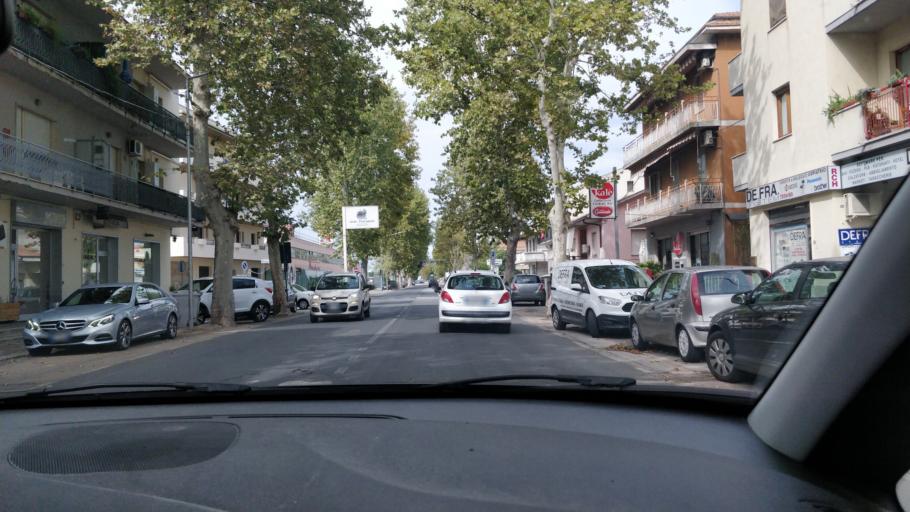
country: IT
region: Abruzzo
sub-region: Provincia di Chieti
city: Sambuceto
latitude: 42.4255
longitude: 14.1856
